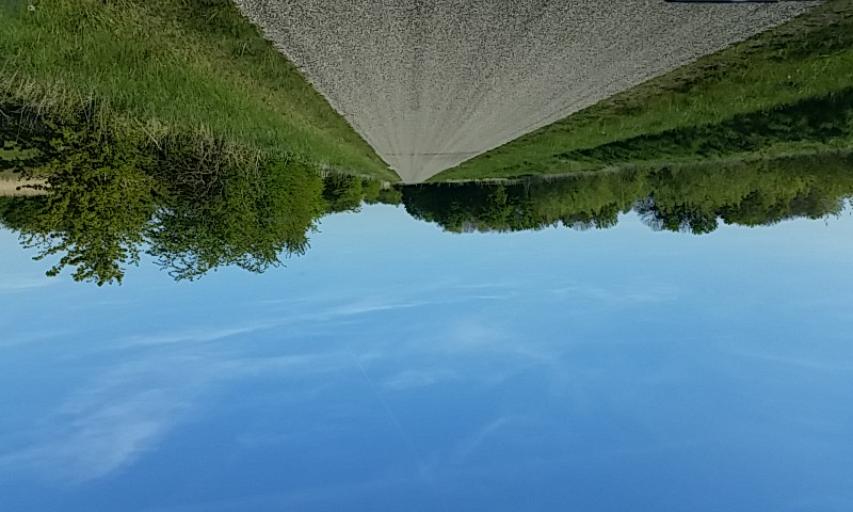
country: NL
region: Zeeland
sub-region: Gemeente Borsele
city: Borssele
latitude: 51.3250
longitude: 3.7278
